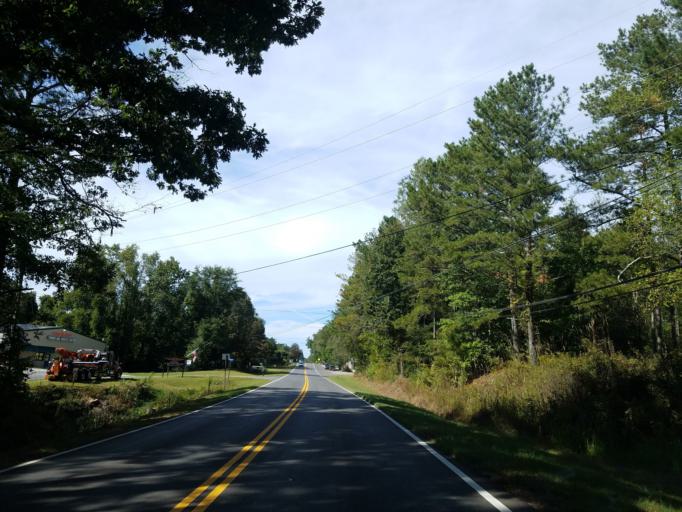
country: US
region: Georgia
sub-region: Pickens County
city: Jasper
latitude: 34.4349
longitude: -84.3960
